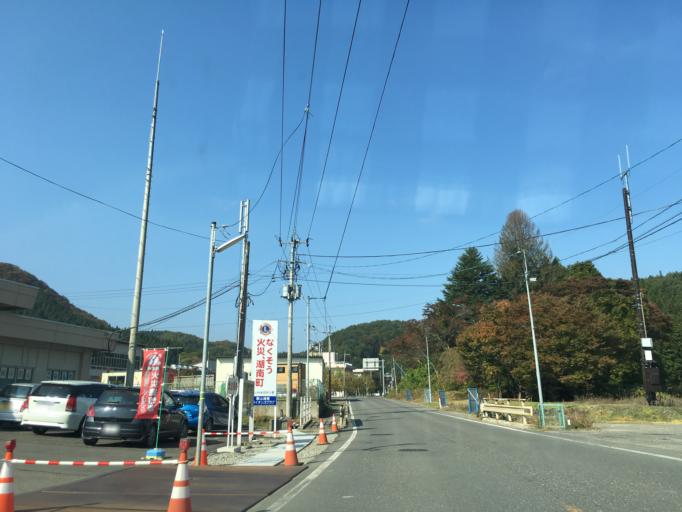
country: JP
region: Fukushima
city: Inawashiro
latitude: 37.3824
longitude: 140.1159
